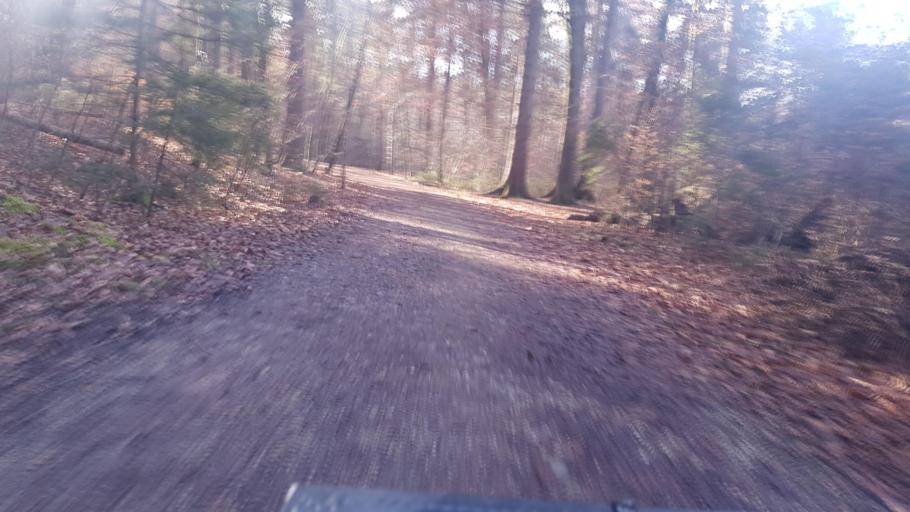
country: DE
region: Bavaria
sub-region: Upper Bavaria
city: Gauting
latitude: 48.0431
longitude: 11.3669
